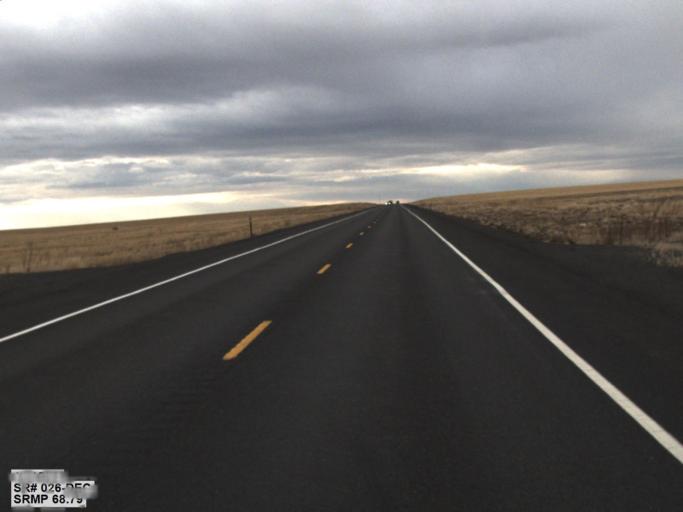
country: US
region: Washington
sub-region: Franklin County
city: Connell
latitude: 46.7946
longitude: -118.5853
